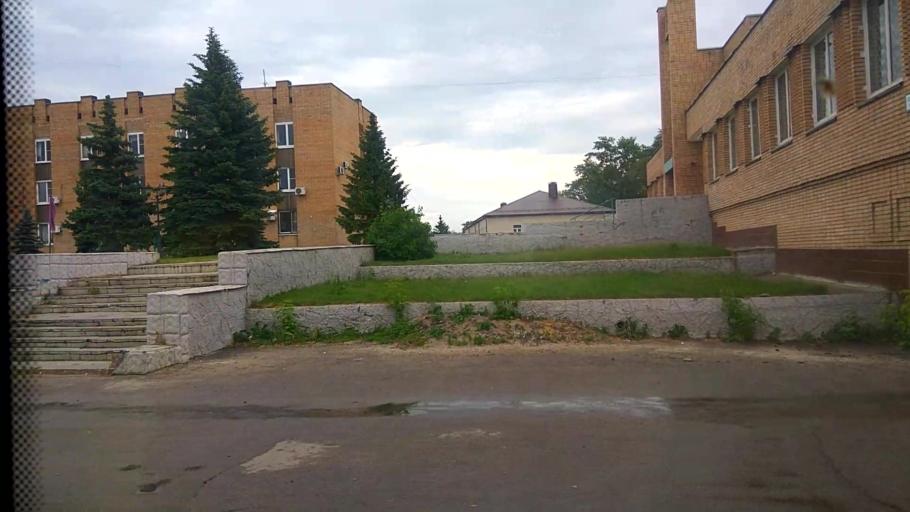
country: RU
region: Moskovskaya
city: Ozery
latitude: 54.8536
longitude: 38.5687
